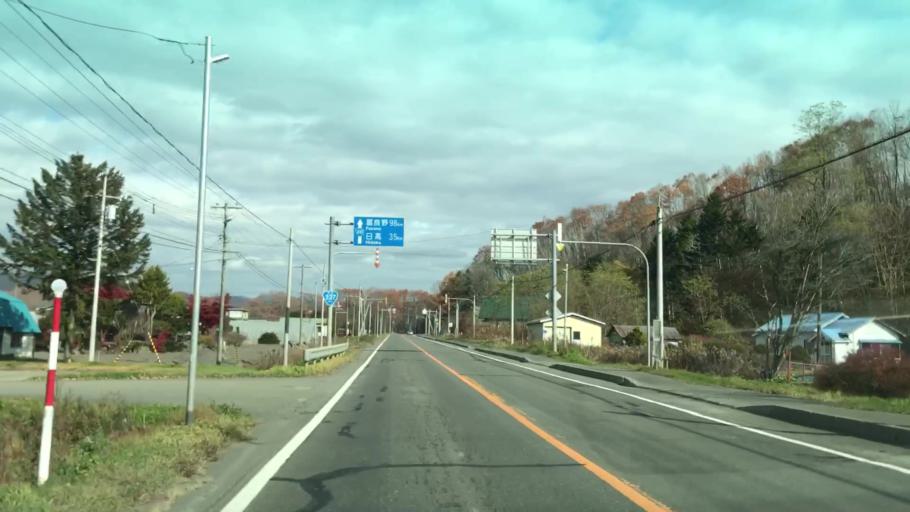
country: JP
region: Hokkaido
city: Shizunai-furukawacho
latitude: 42.6800
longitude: 142.1989
